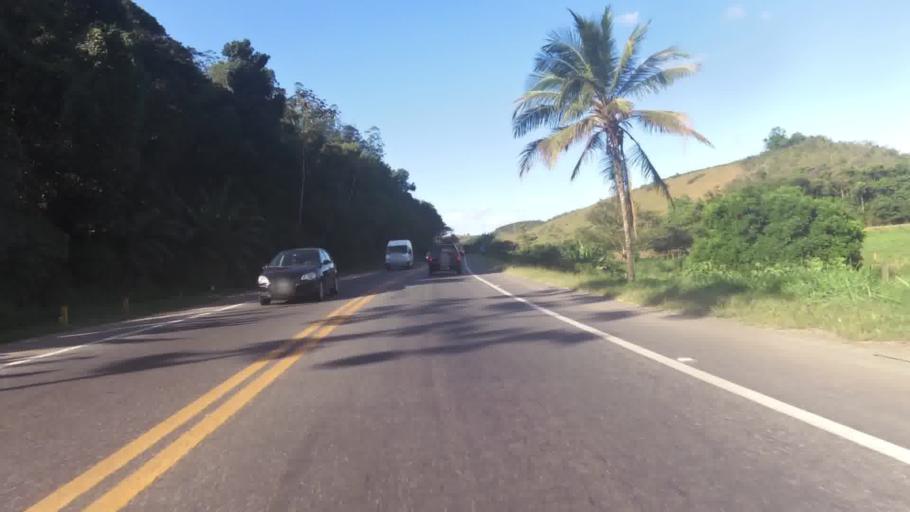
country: BR
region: Espirito Santo
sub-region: Iconha
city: Iconha
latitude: -20.8198
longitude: -40.8461
